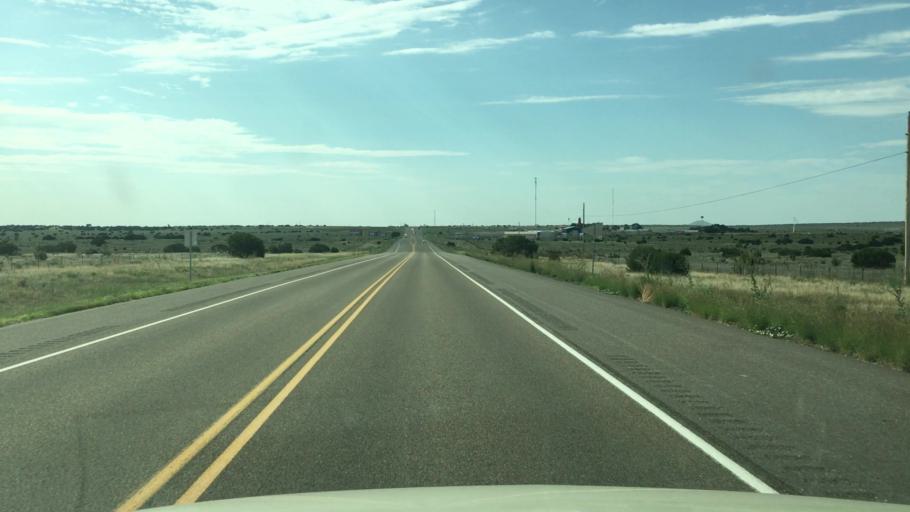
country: US
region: New Mexico
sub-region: Torrance County
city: Moriarty
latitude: 35.0230
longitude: -105.6726
